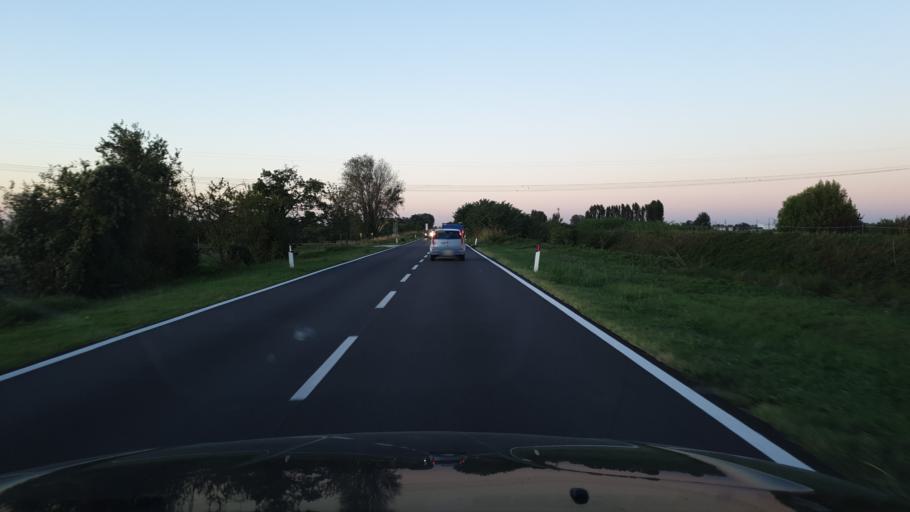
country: IT
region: Emilia-Romagna
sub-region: Provincia di Bologna
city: Ca De Fabbri
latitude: 44.6034
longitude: 11.4416
